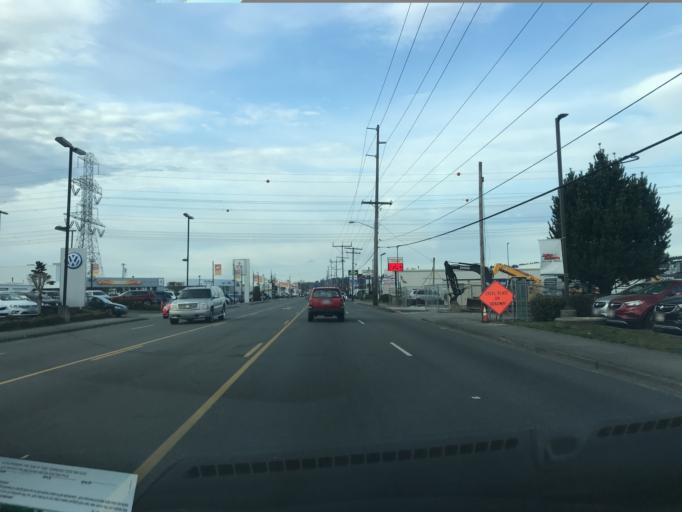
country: US
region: Washington
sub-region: King County
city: Auburn
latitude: 47.3353
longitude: -122.2222
